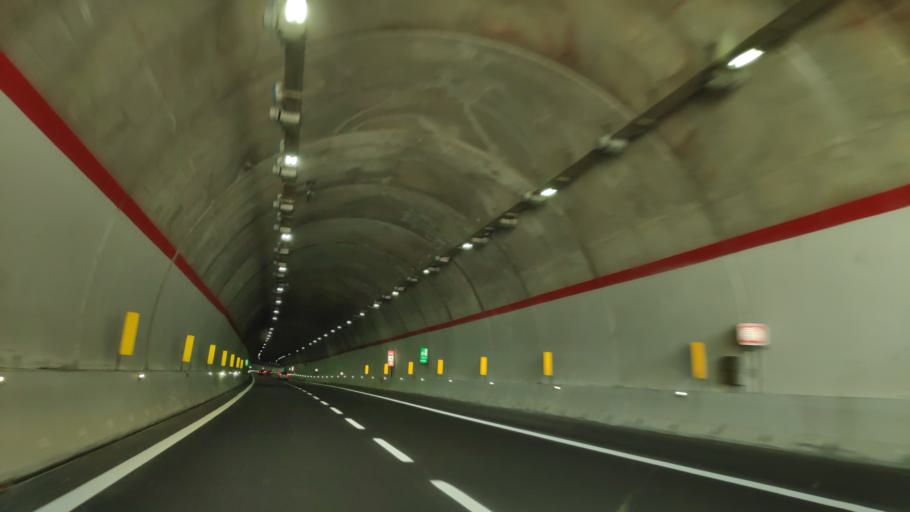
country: IT
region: Basilicate
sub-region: Provincia di Potenza
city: Lagonegro
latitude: 40.1110
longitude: 15.7913
